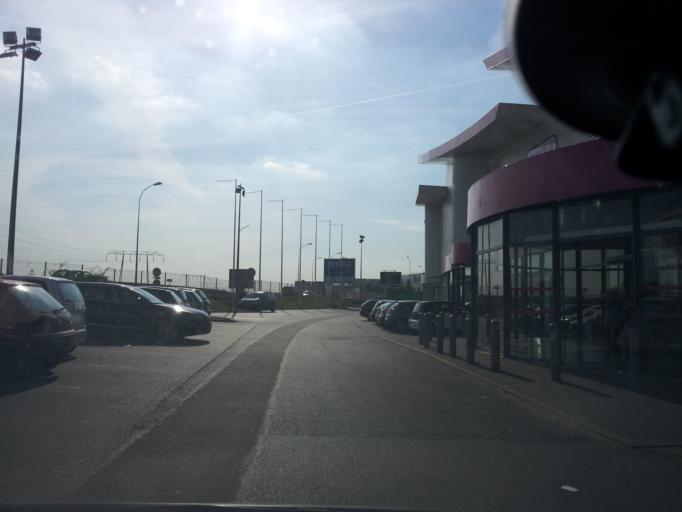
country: FR
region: Ile-de-France
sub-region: Departement de l'Essonne
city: Fleury-Merogis
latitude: 48.6200
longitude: 2.3522
